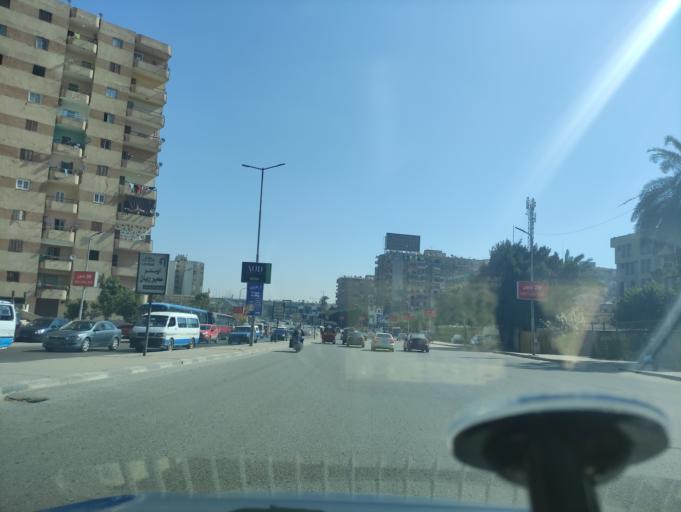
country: EG
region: Muhafazat al Qahirah
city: Cairo
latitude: 30.0565
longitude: 31.2974
